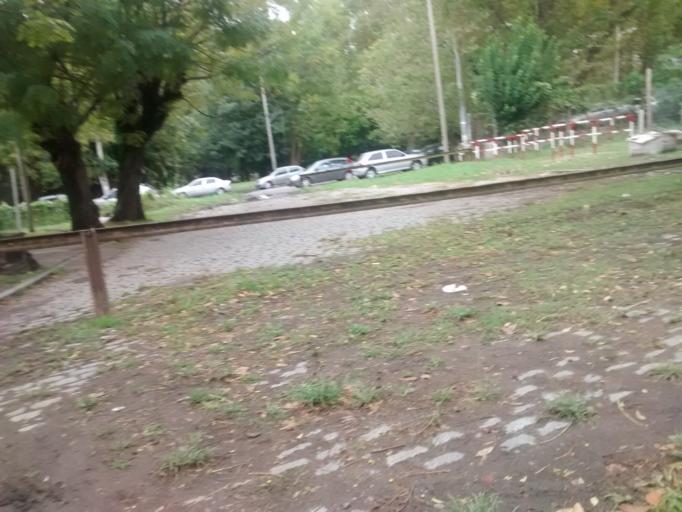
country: AR
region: Buenos Aires
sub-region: Partido de La Plata
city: La Plata
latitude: -34.9028
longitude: -57.9370
